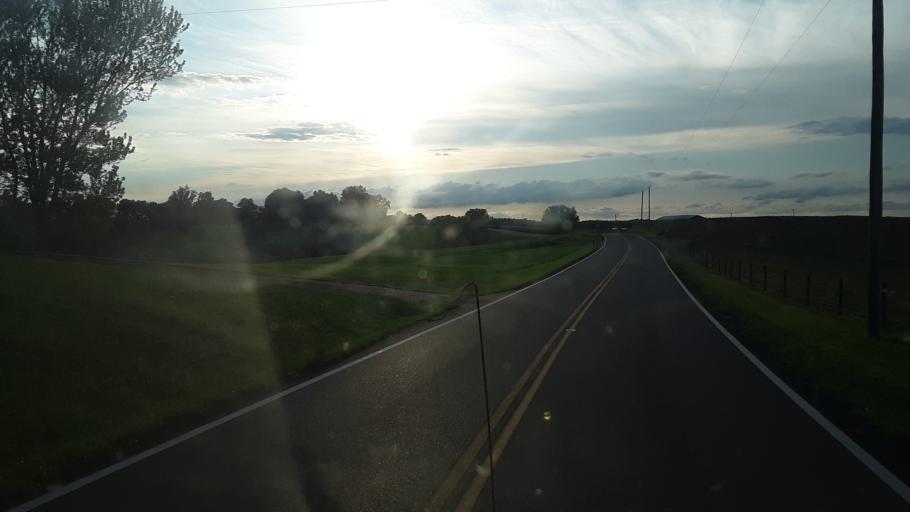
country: US
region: Ohio
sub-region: Harrison County
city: Cadiz
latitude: 40.3965
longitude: -81.0089
